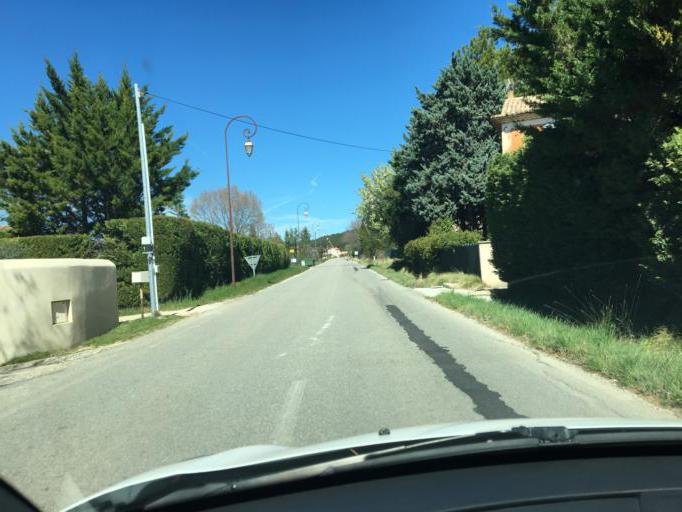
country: FR
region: Provence-Alpes-Cote d'Azur
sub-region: Departement du Vaucluse
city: Gargas
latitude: 43.8821
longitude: 5.3430
